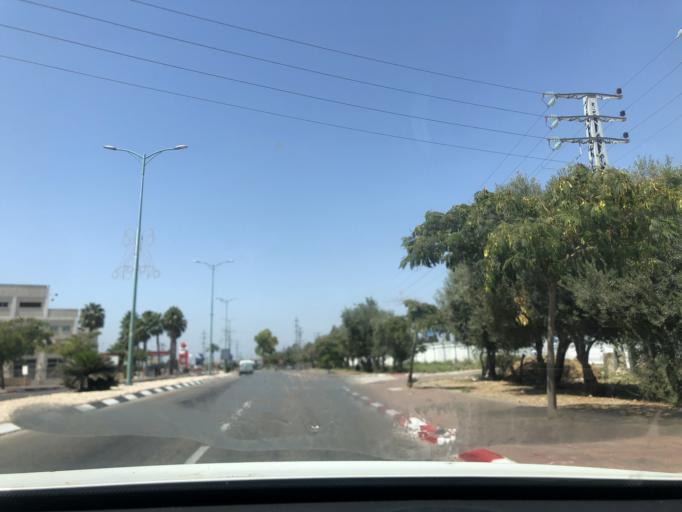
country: IL
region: Central District
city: Lod
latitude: 31.9654
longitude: 34.9002
